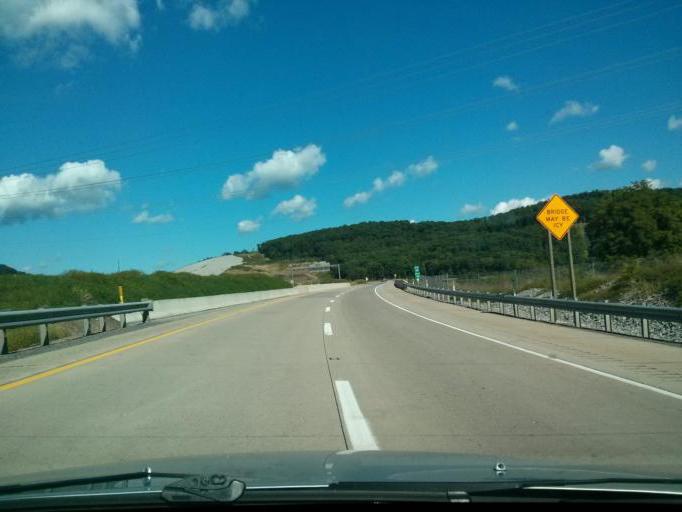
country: US
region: Pennsylvania
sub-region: Centre County
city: Park Forest Village
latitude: 40.8257
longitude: -77.9546
